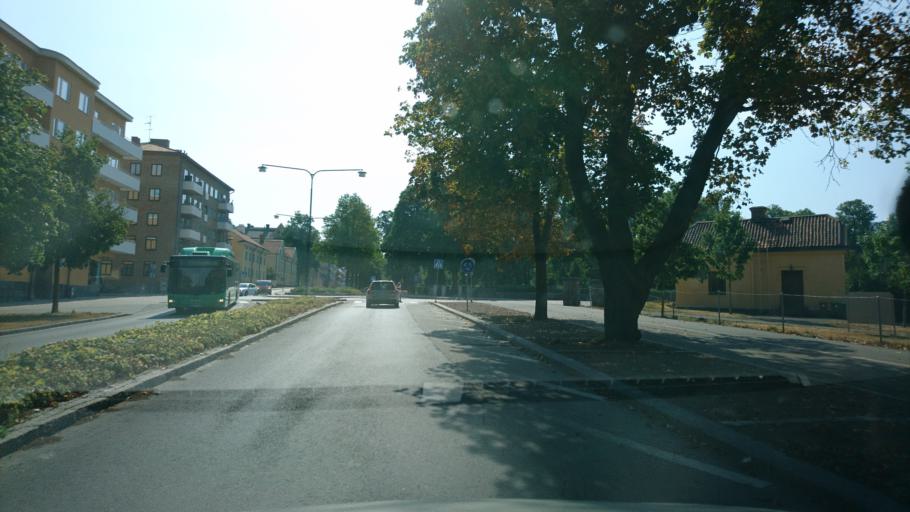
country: SE
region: Uppsala
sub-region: Uppsala Kommun
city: Uppsala
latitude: 59.8581
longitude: 17.6244
